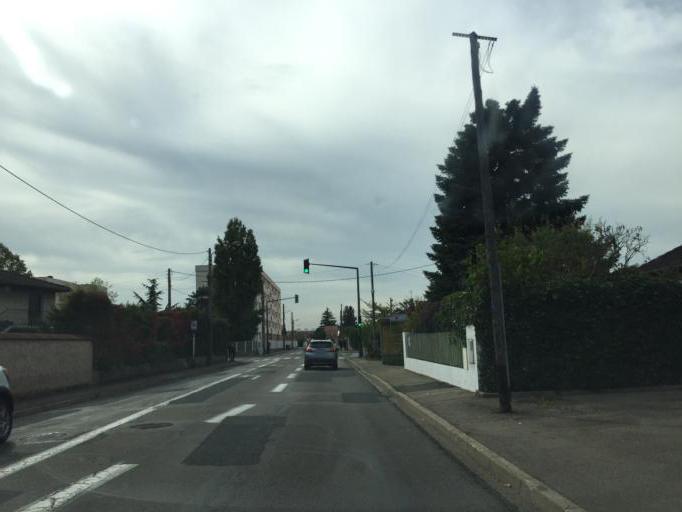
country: FR
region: Rhone-Alpes
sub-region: Departement du Rhone
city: Meyzieu
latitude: 45.7812
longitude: 5.0012
